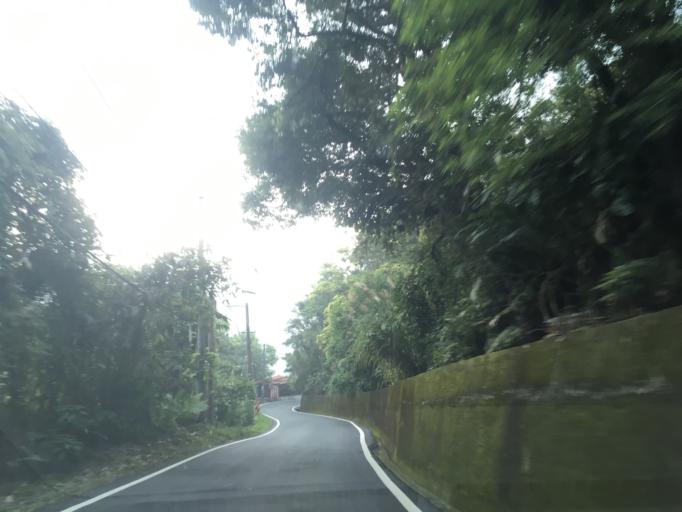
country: TW
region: Taiwan
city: Daxi
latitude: 24.8814
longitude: 121.3058
